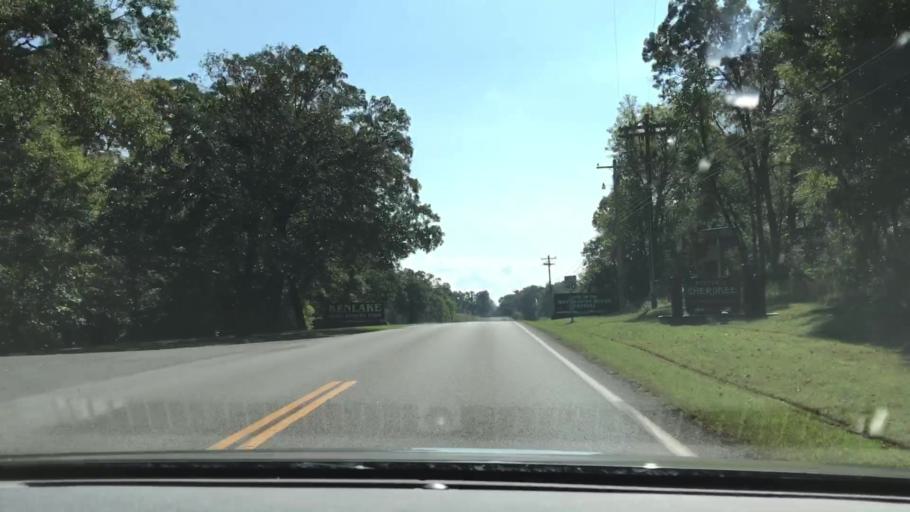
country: US
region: Kentucky
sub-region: Marshall County
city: Benton
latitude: 36.7731
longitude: -88.1395
